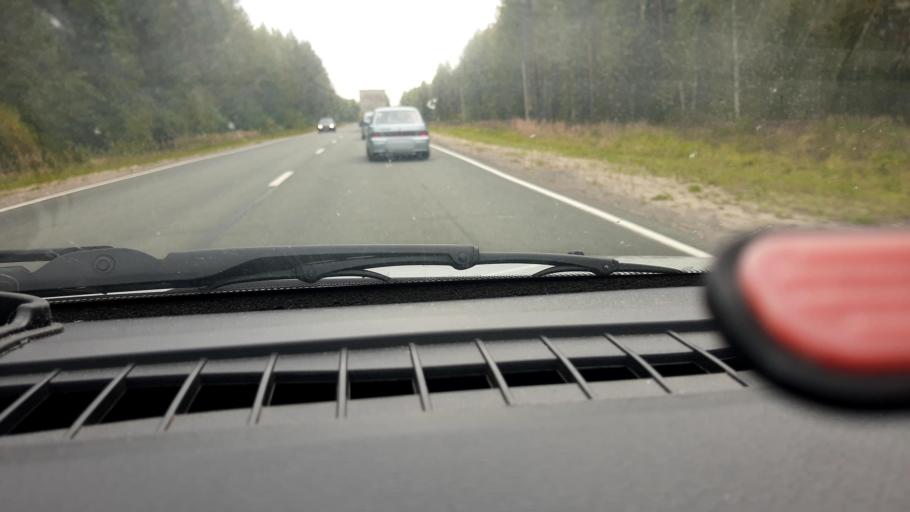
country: RU
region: Nizjnij Novgorod
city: Uren'
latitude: 57.3822
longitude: 45.6885
